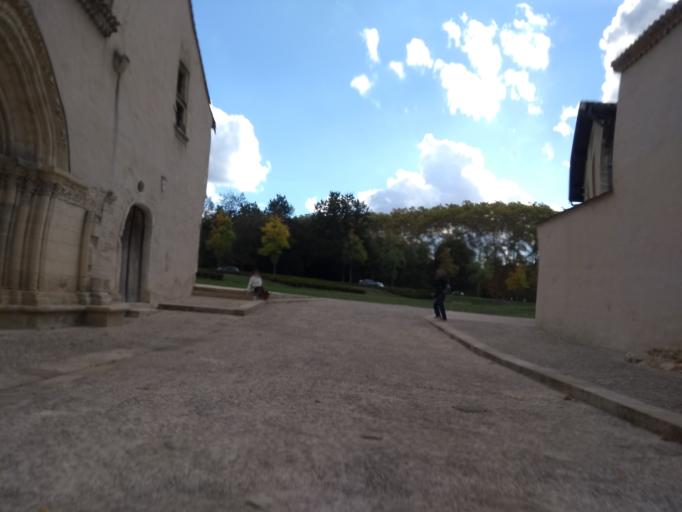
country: FR
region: Aquitaine
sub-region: Departement de la Gironde
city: Gradignan
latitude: 44.7652
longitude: -0.6193
